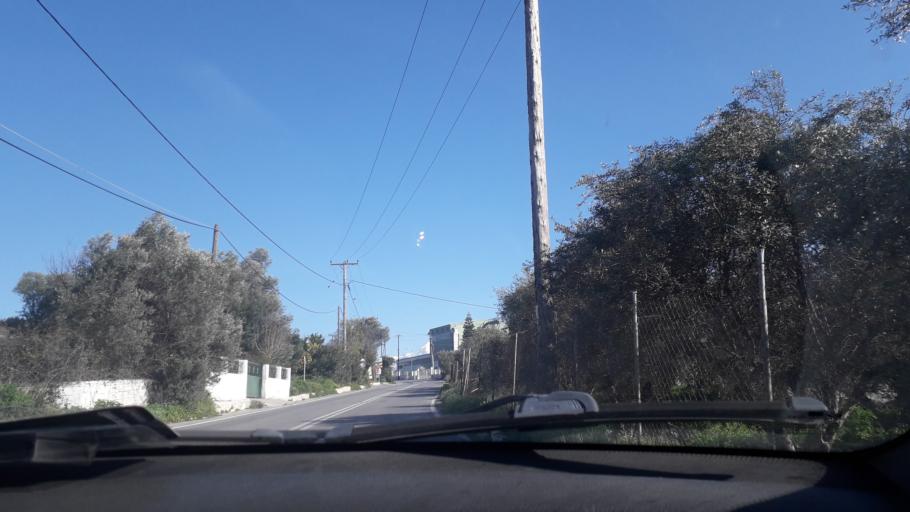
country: GR
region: Crete
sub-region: Nomos Rethymnis
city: Rethymno
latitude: 35.3599
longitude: 24.5489
